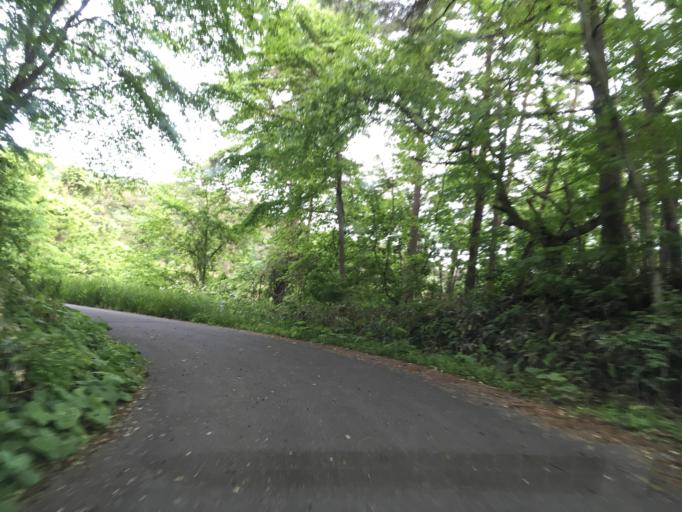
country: JP
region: Iwate
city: Mizusawa
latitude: 39.1301
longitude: 141.2982
